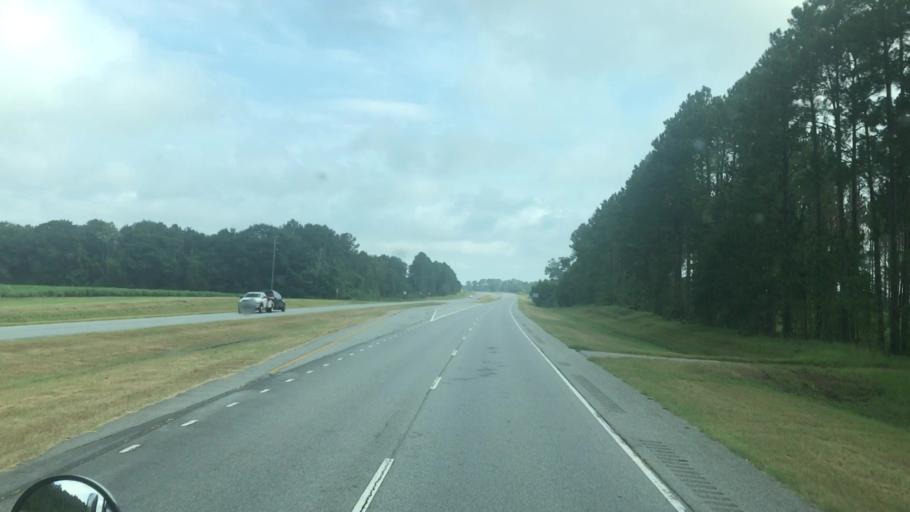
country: US
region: Georgia
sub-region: Miller County
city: Colquitt
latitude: 31.1994
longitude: -84.7690
